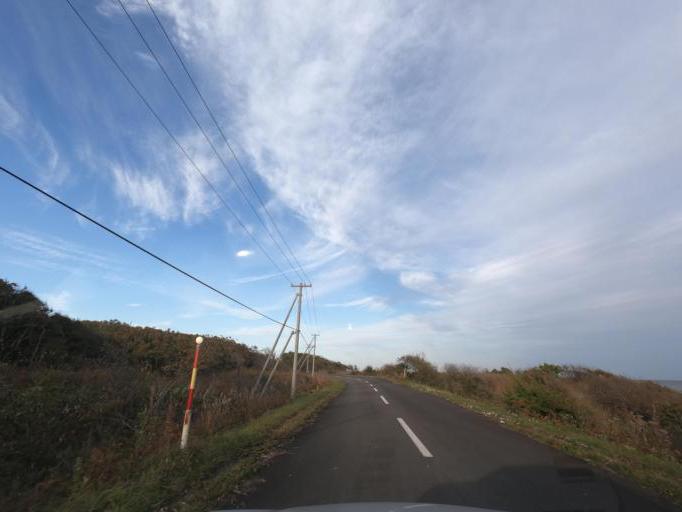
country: JP
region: Hokkaido
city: Obihiro
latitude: 42.5430
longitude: 143.4926
